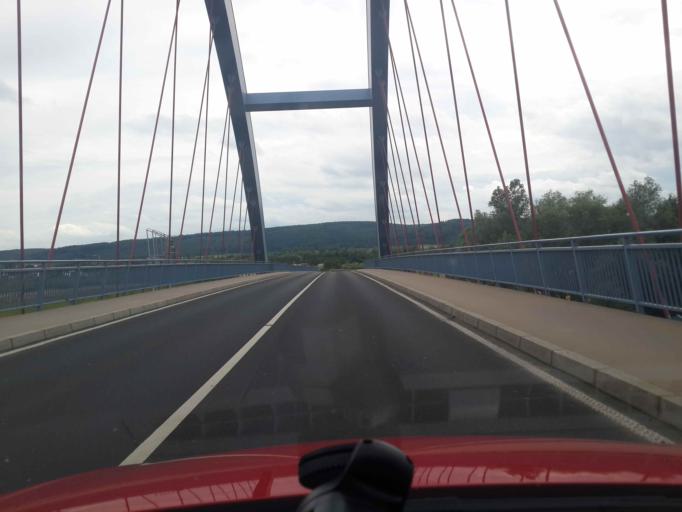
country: DE
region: Bavaria
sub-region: Regierungsbezirk Unterfranken
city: Sulzbach am Main
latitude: 49.8954
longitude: 9.1513
